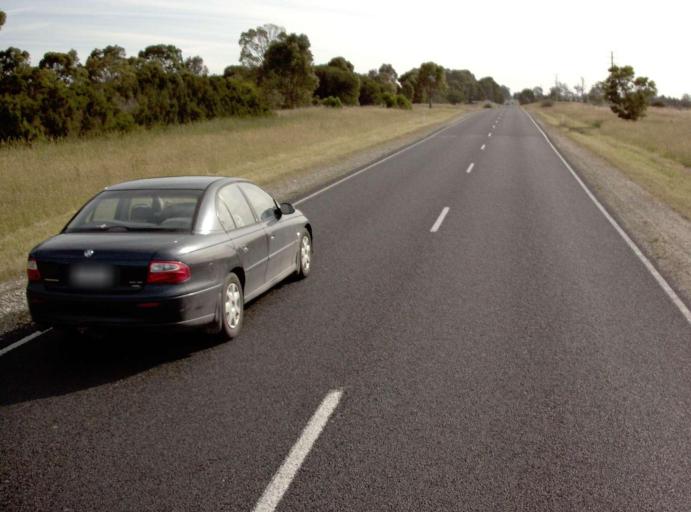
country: AU
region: Victoria
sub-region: Latrobe
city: Traralgon
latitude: -38.1112
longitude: 146.5853
